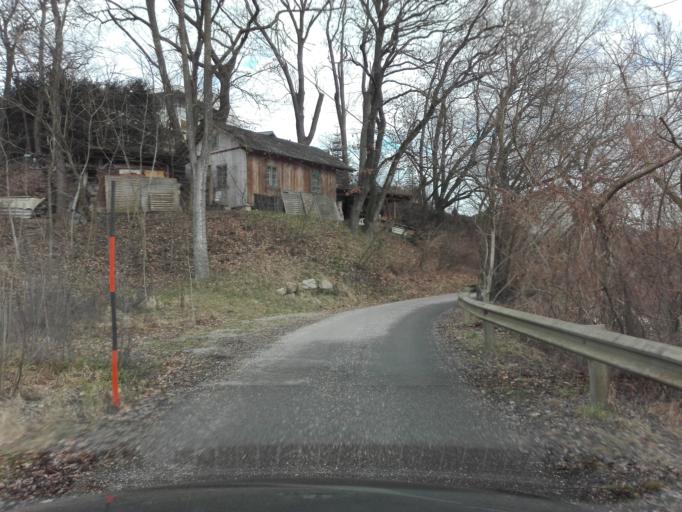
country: AT
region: Upper Austria
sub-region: Politischer Bezirk Perg
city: Perg
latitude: 48.2626
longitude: 14.5824
